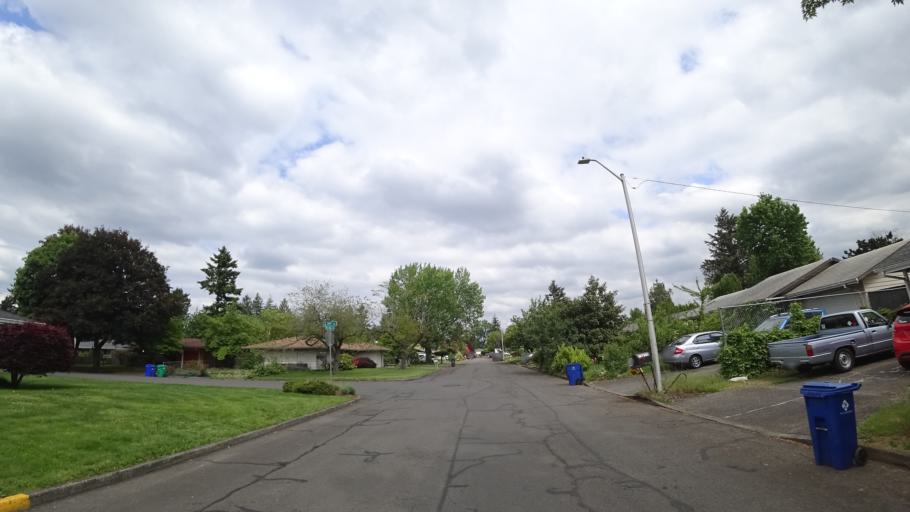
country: US
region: Oregon
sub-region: Multnomah County
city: Gresham
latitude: 45.5114
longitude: -122.4793
